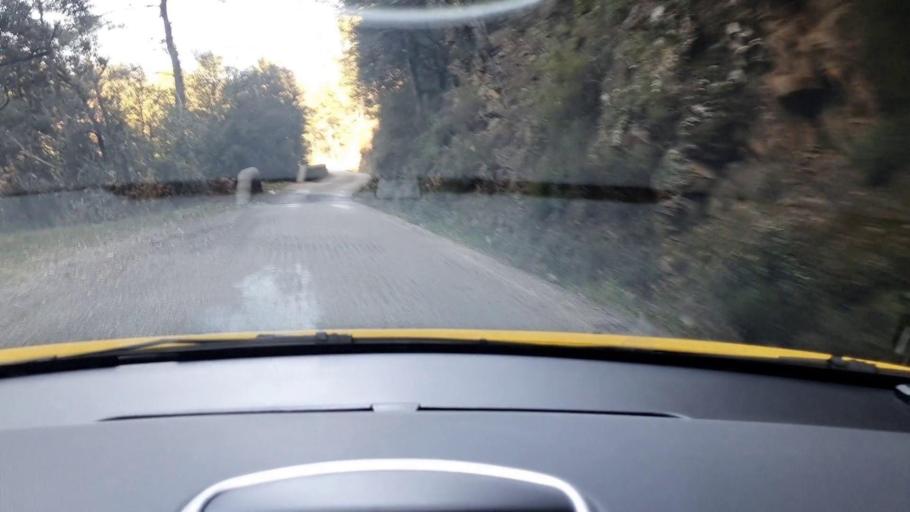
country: FR
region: Languedoc-Roussillon
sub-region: Departement du Gard
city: Branoux-les-Taillades
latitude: 44.2745
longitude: 3.9778
